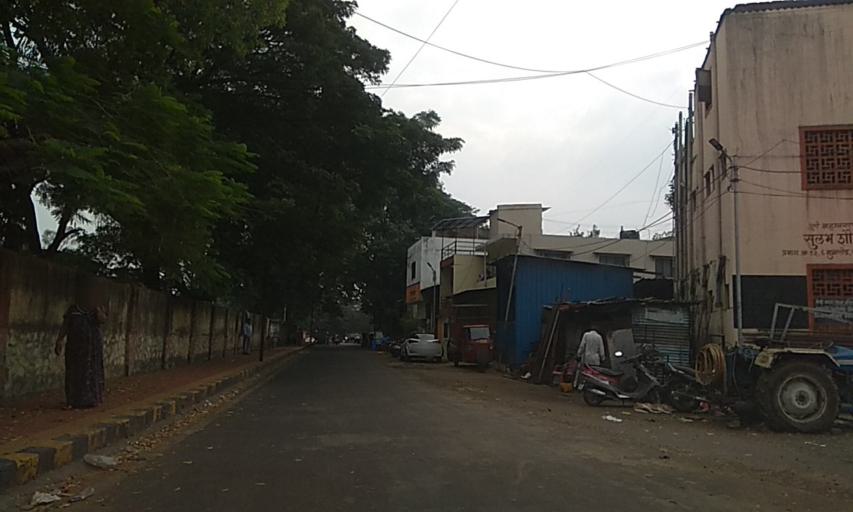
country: IN
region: Maharashtra
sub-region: Pune Division
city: Khadki
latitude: 18.5521
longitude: 73.8545
